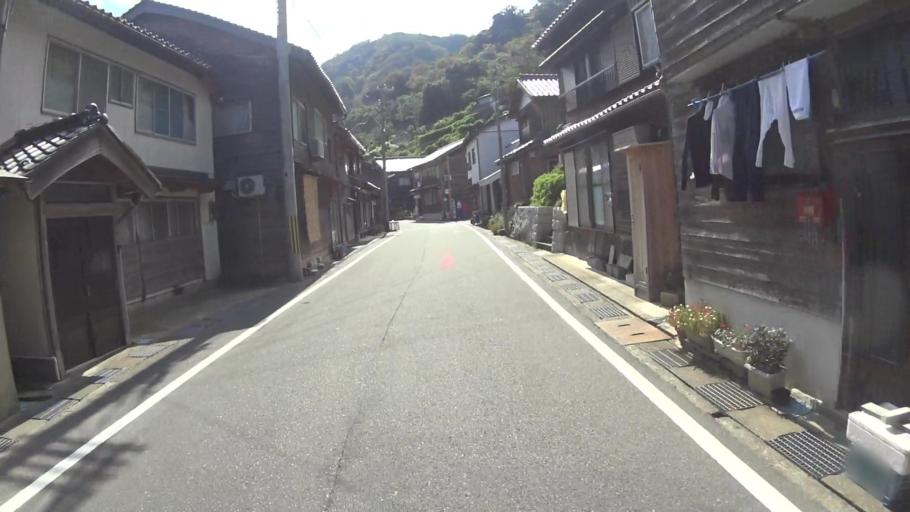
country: JP
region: Kyoto
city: Miyazu
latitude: 35.7538
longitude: 135.2516
